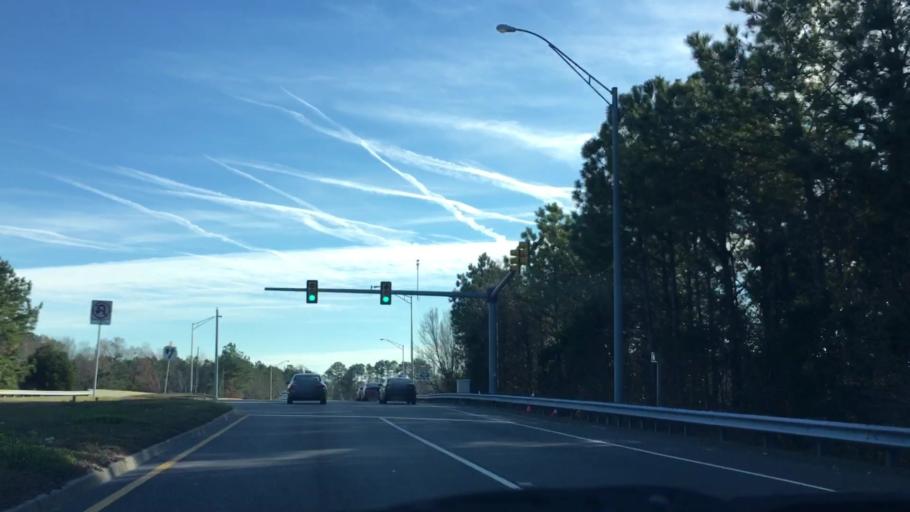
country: US
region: Virginia
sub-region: City of Portsmouth
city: Portsmouth Heights
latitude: 36.8686
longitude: -76.4226
